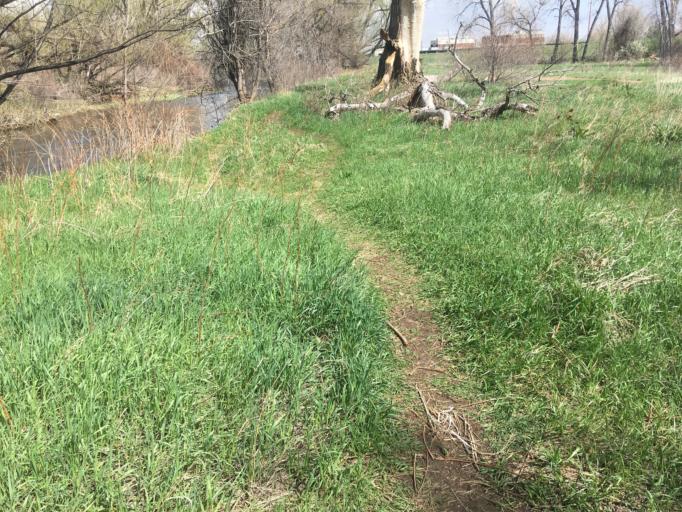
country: US
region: Colorado
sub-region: Boulder County
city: Gunbarrel
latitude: 40.0503
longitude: -105.1852
